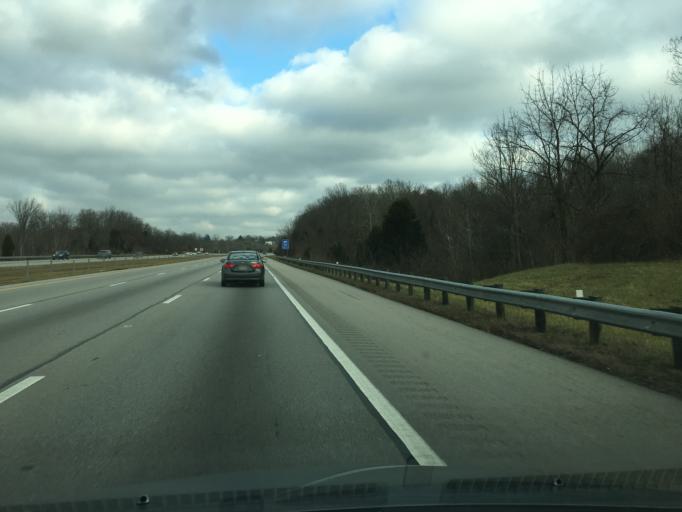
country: US
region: Ohio
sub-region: Hamilton County
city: Dent
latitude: 39.2238
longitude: -84.6606
